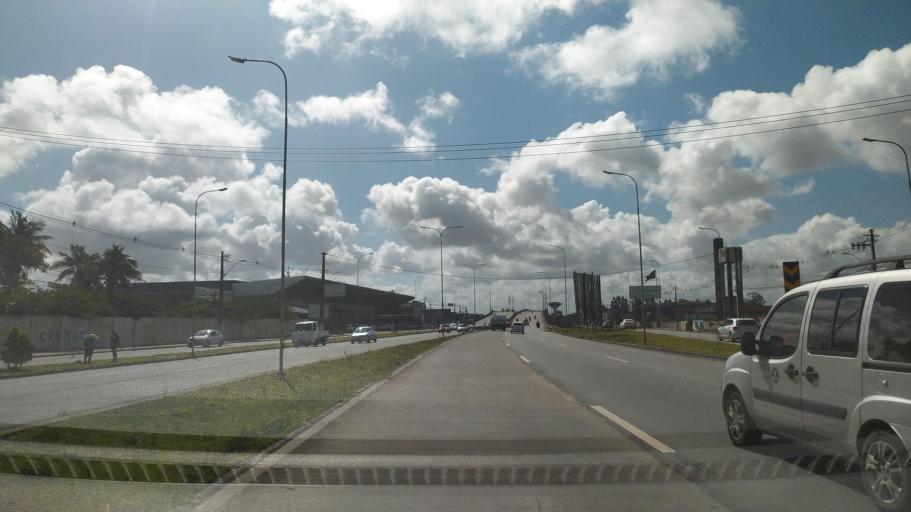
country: BR
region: Alagoas
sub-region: Satuba
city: Satuba
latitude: -9.5697
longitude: -35.7750
